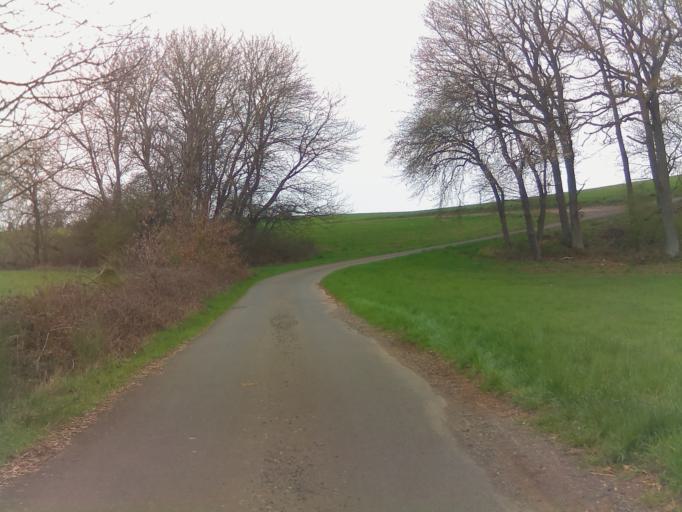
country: DE
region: Rheinland-Pfalz
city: Gerach
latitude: 49.7533
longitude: 7.3225
